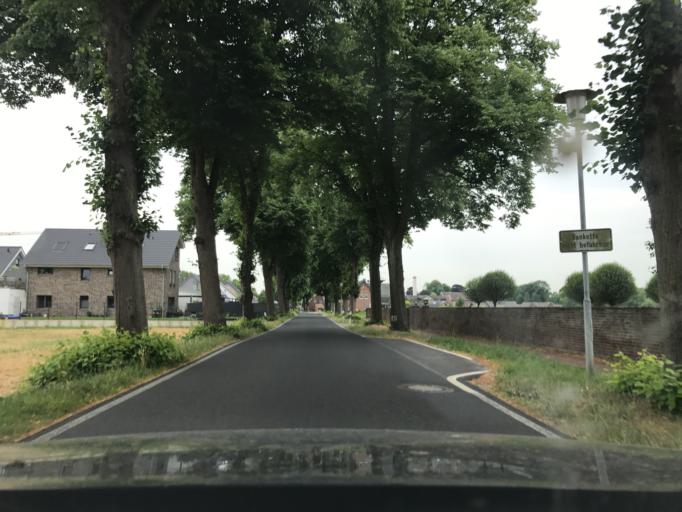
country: DE
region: North Rhine-Westphalia
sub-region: Regierungsbezirk Dusseldorf
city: Grefrath
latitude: 51.3479
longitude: 6.3642
